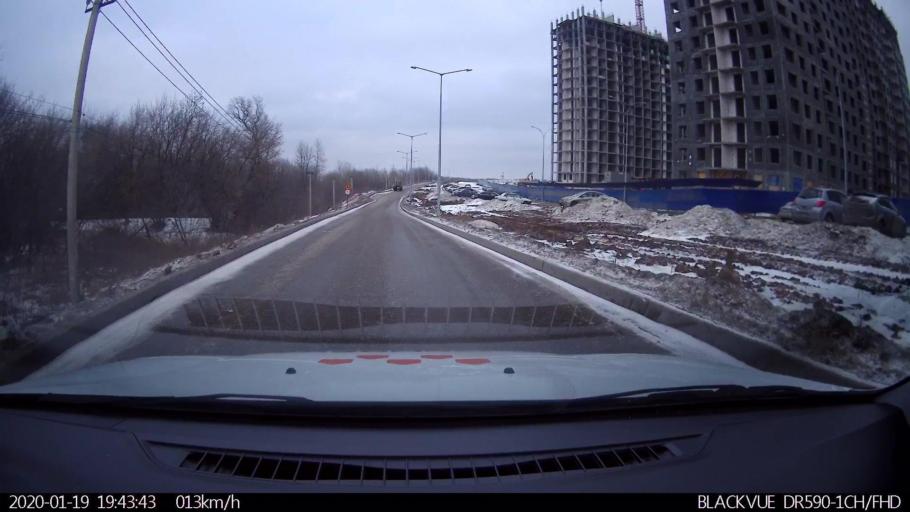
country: RU
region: Nizjnij Novgorod
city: Afonino
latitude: 56.2491
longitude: 44.0496
